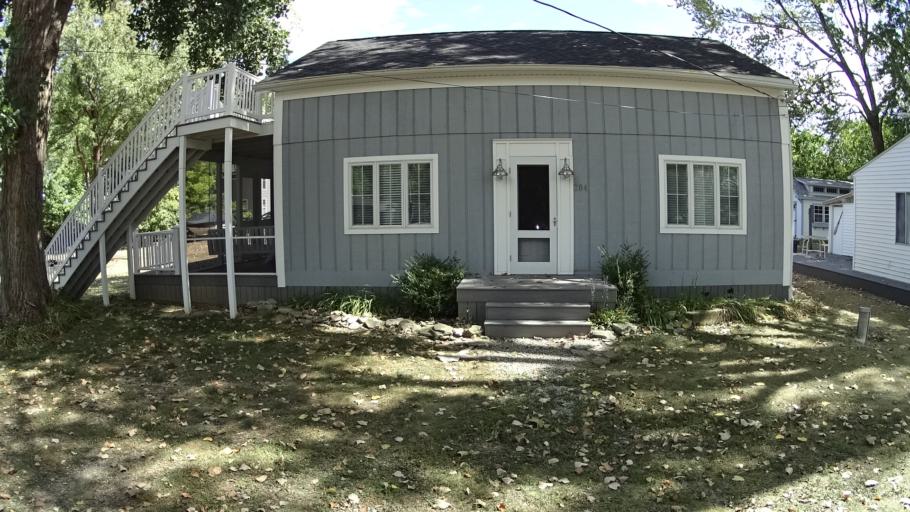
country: US
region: Ohio
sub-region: Erie County
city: Sandusky
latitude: 41.6102
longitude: -82.6954
